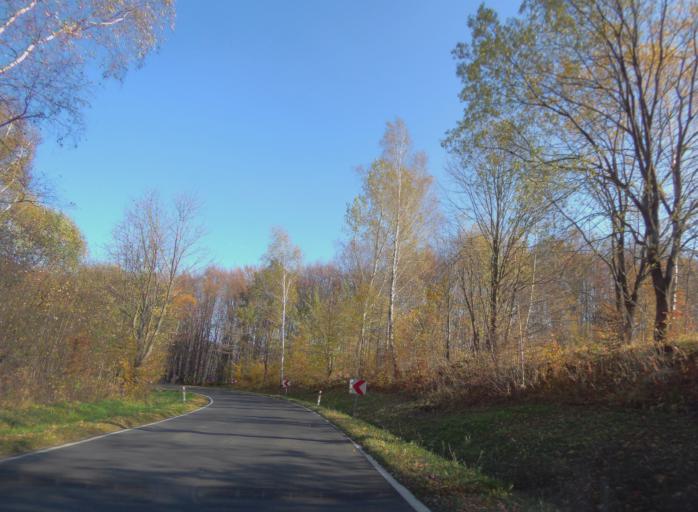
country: PL
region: Subcarpathian Voivodeship
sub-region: Powiat leski
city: Polanczyk
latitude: 49.3916
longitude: 22.4327
